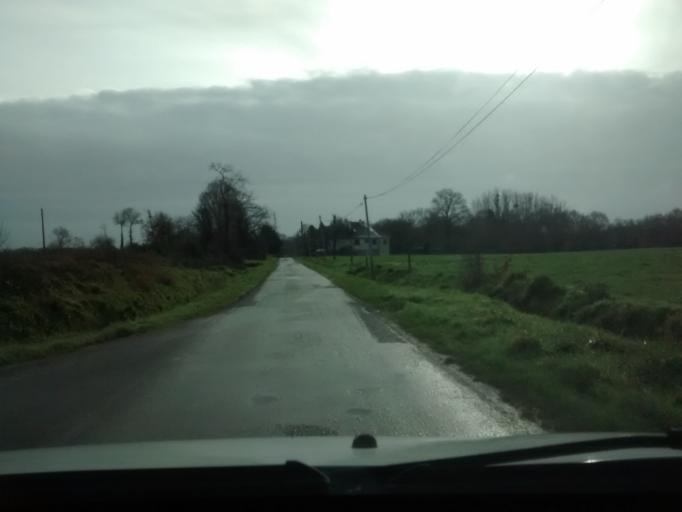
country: FR
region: Brittany
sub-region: Departement d'Ille-et-Vilaine
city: Vezin-le-Coquet
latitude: 48.1416
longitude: -1.7472
